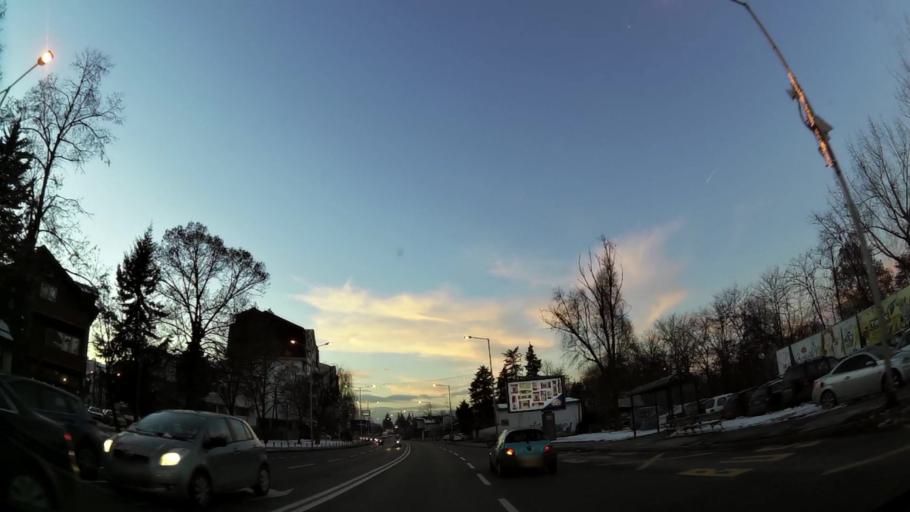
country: MK
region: Karpos
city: Skopje
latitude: 42.0058
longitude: 21.4165
